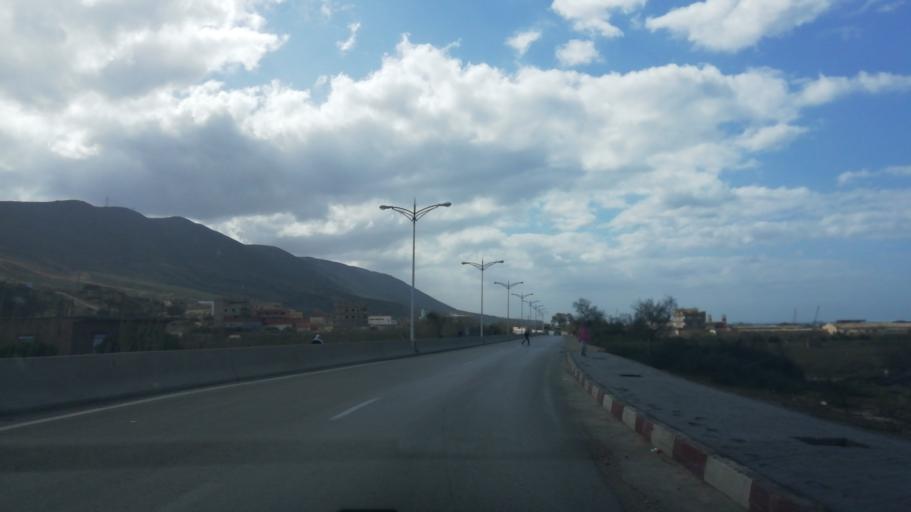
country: DZ
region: Mostaganem
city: Mostaganem
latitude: 36.0267
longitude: 0.1350
